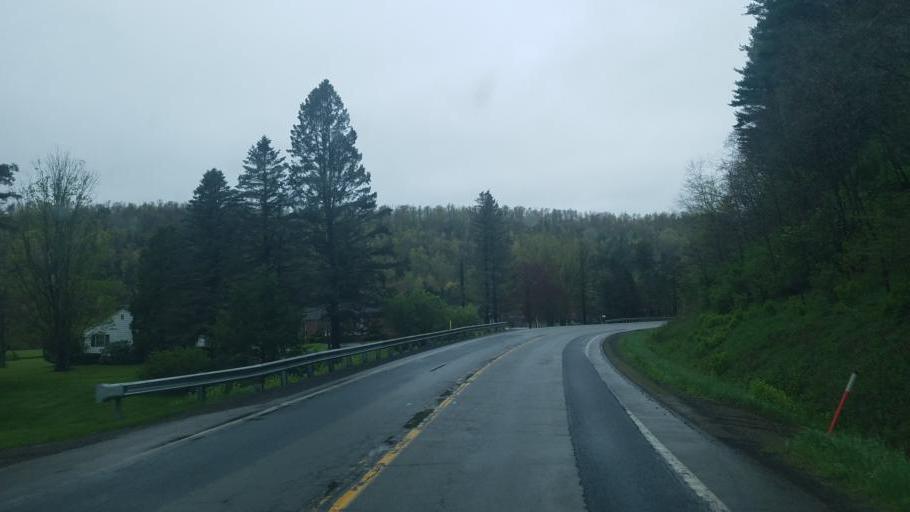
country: US
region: Pennsylvania
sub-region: Potter County
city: Coudersport
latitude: 41.8132
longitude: -77.9921
